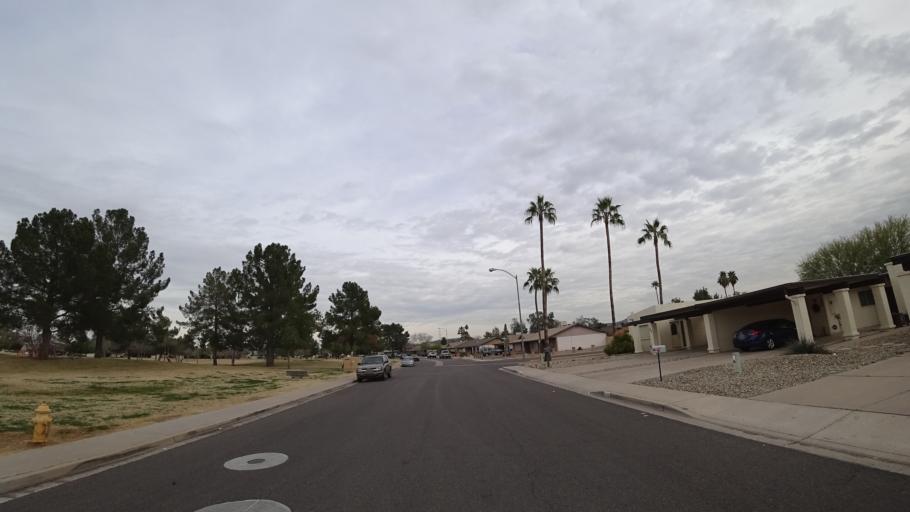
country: US
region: Arizona
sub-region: Maricopa County
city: Glendale
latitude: 33.6144
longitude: -112.1226
